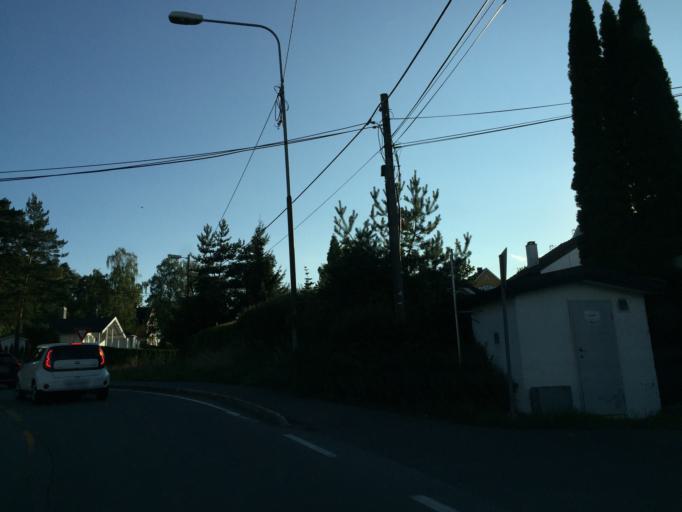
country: NO
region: Akershus
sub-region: Baerum
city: Lysaker
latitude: 59.9059
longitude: 10.6019
